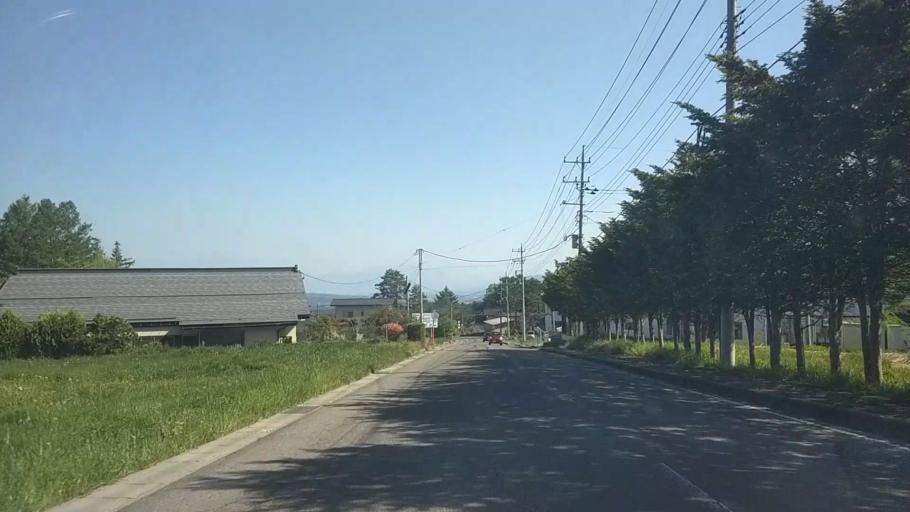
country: JP
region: Yamanashi
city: Nirasaki
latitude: 35.9001
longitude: 138.4098
